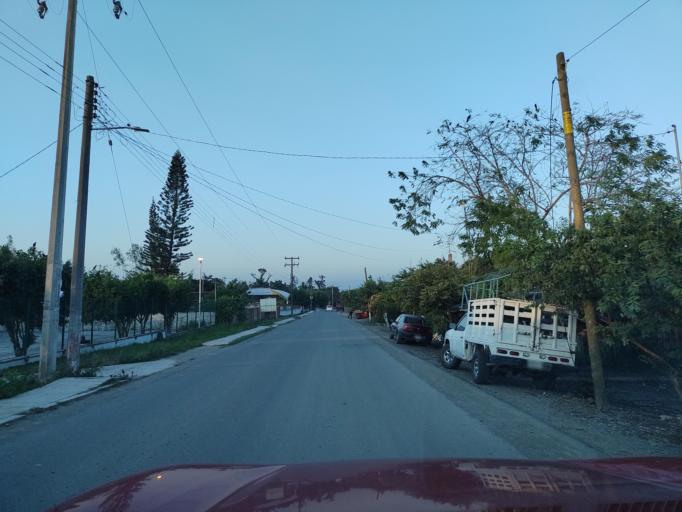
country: MX
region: Veracruz
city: Agua Dulce
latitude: 20.3135
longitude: -97.2726
